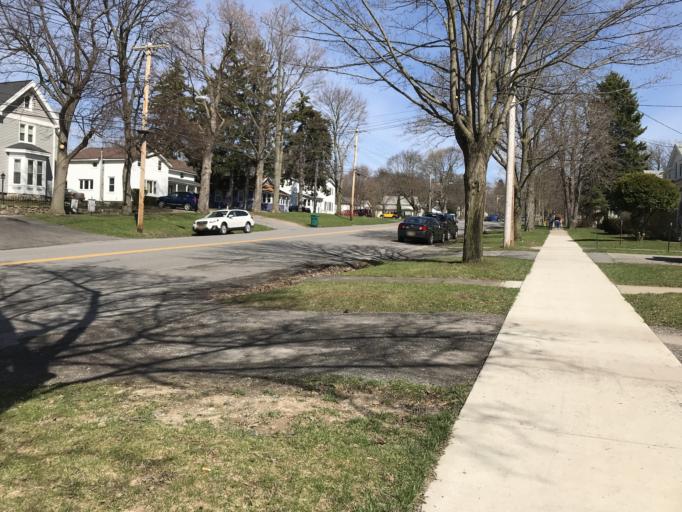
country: US
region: New York
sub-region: Livingston County
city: Geneseo
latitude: 42.7996
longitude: -77.8127
